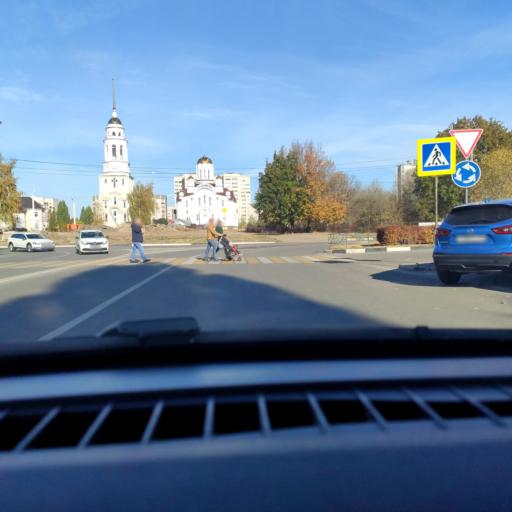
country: RU
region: Voronezj
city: Podgornoye
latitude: 51.7150
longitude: 39.1733
